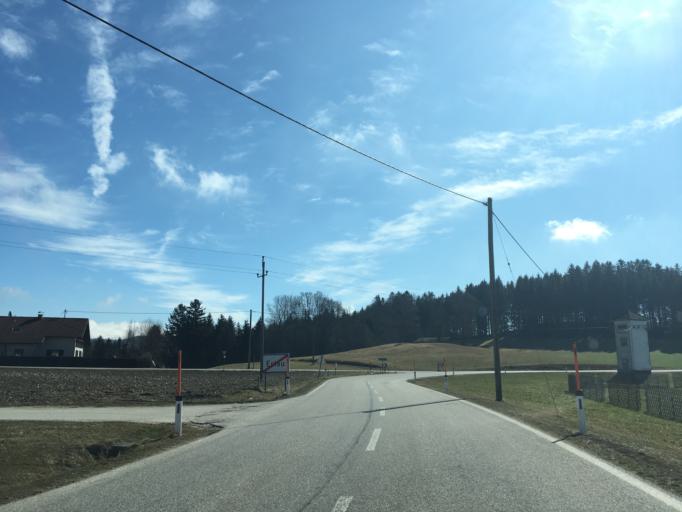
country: AT
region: Upper Austria
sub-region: Politischer Bezirk Perg
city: Sankt Georgen am Walde
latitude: 48.3294
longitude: 14.9132
